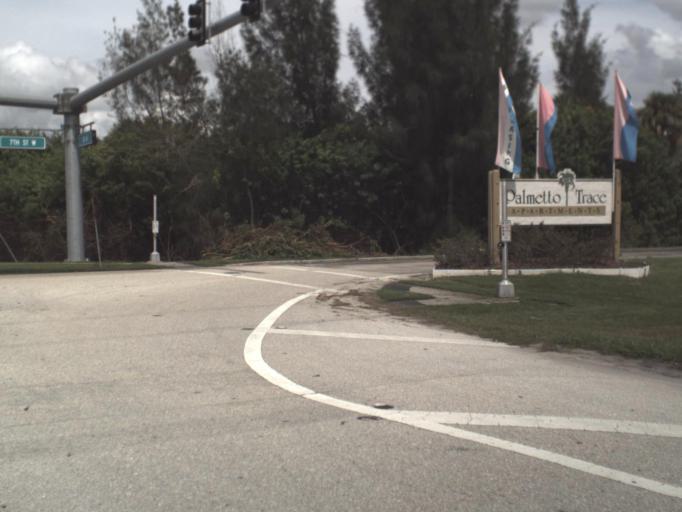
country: US
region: Florida
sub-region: Manatee County
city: Palmetto
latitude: 27.5172
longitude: -82.5630
